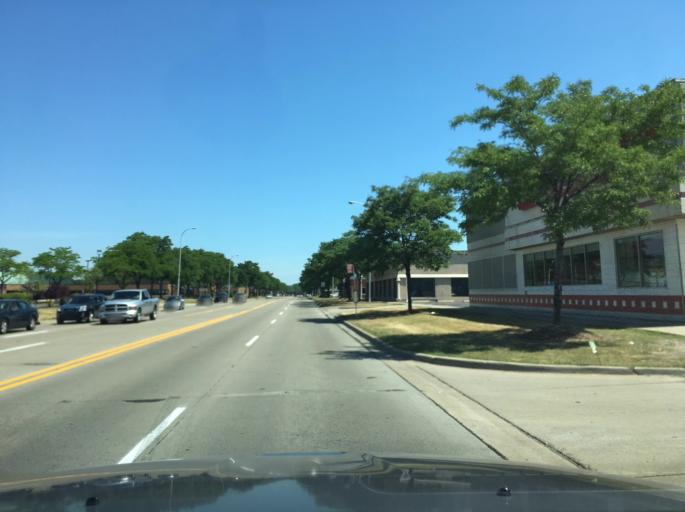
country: US
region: Michigan
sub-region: Macomb County
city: Saint Clair Shores
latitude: 42.4807
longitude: -82.9013
